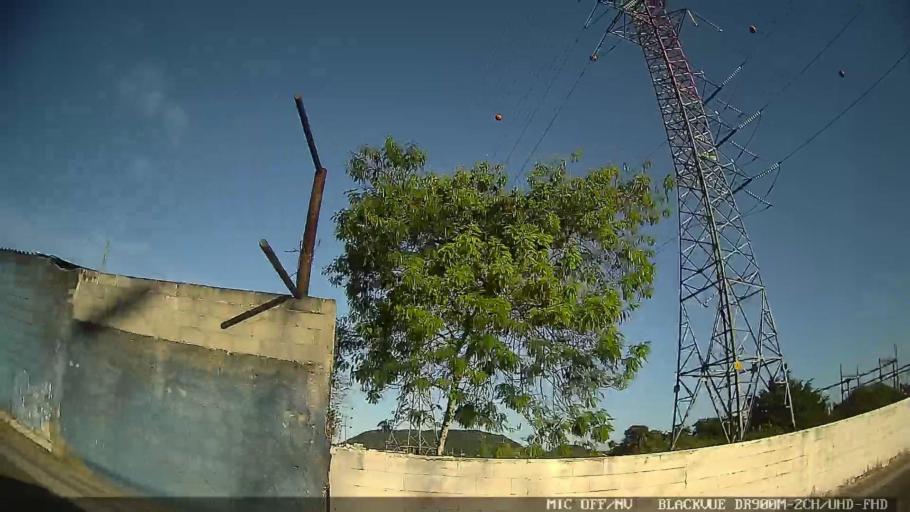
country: BR
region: Sao Paulo
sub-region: Guaruja
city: Guaruja
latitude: -23.9744
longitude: -46.2728
